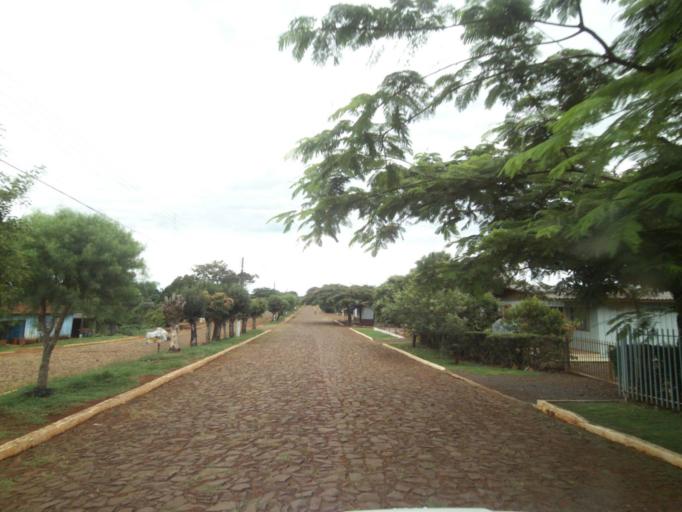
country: BR
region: Parana
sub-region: Guaraniacu
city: Guaraniacu
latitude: -24.9203
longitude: -52.9383
